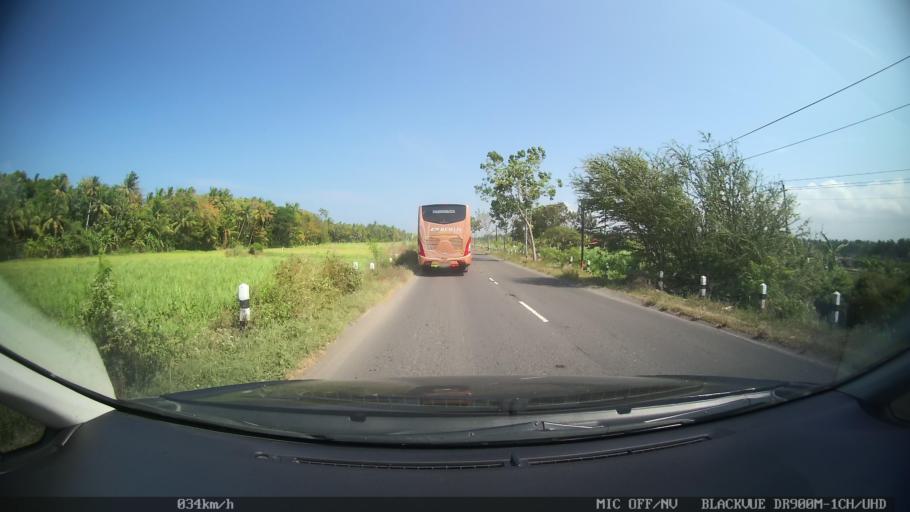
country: ID
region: Daerah Istimewa Yogyakarta
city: Srandakan
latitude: -7.9443
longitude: 110.1720
